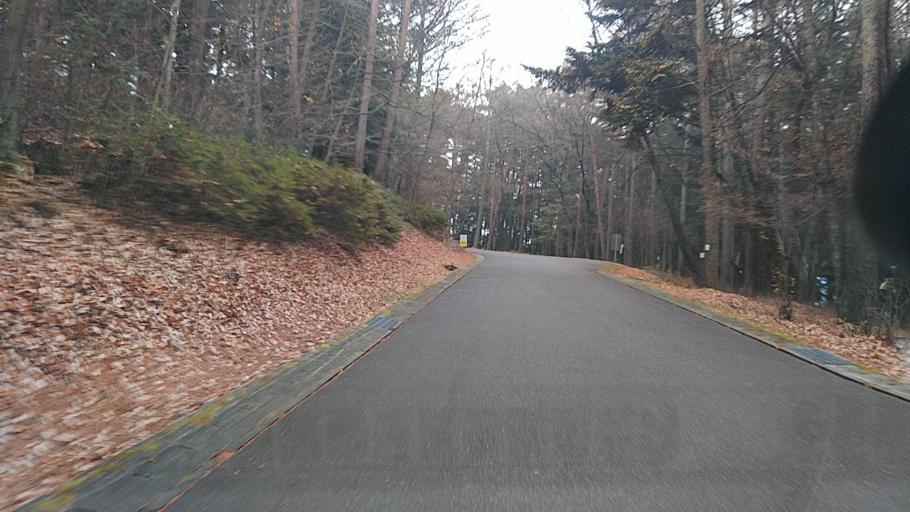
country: JP
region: Nagano
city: Shiojiri
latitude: 36.1449
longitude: 137.9925
